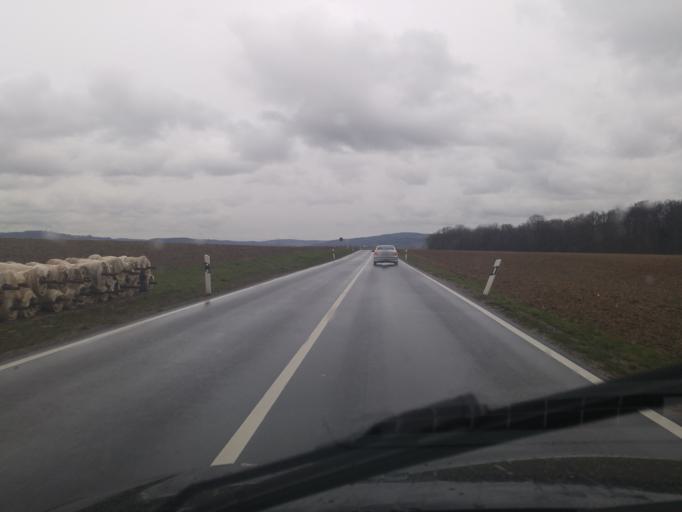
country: DE
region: Baden-Wuerttemberg
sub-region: Regierungsbezirk Stuttgart
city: Affalterbach
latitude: 48.9077
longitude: 9.3419
